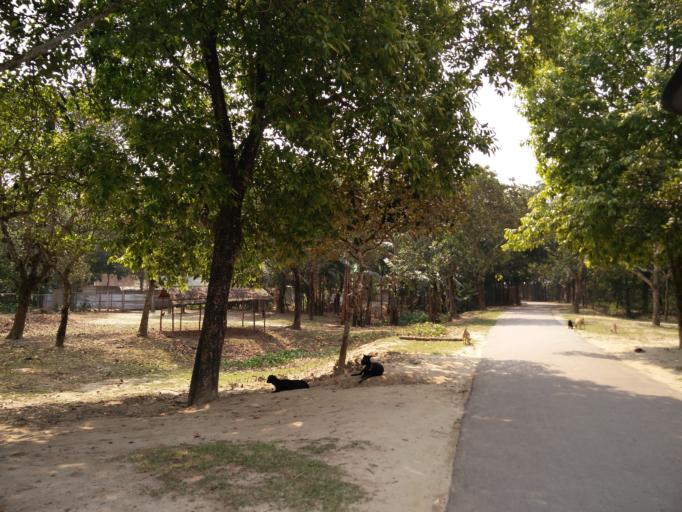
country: BD
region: Dhaka
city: Muktagacha
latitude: 24.9113
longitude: 90.2543
